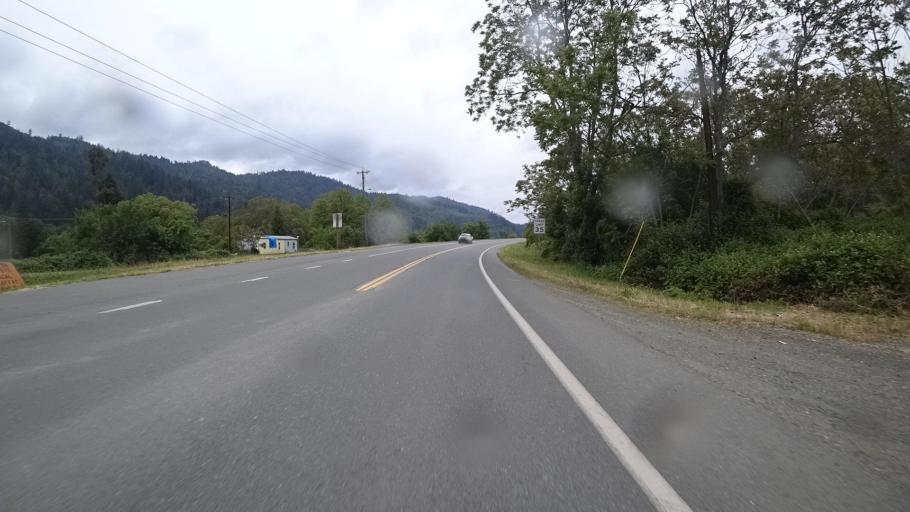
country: US
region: California
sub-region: Humboldt County
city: Willow Creek
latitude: 41.0577
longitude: -123.6833
